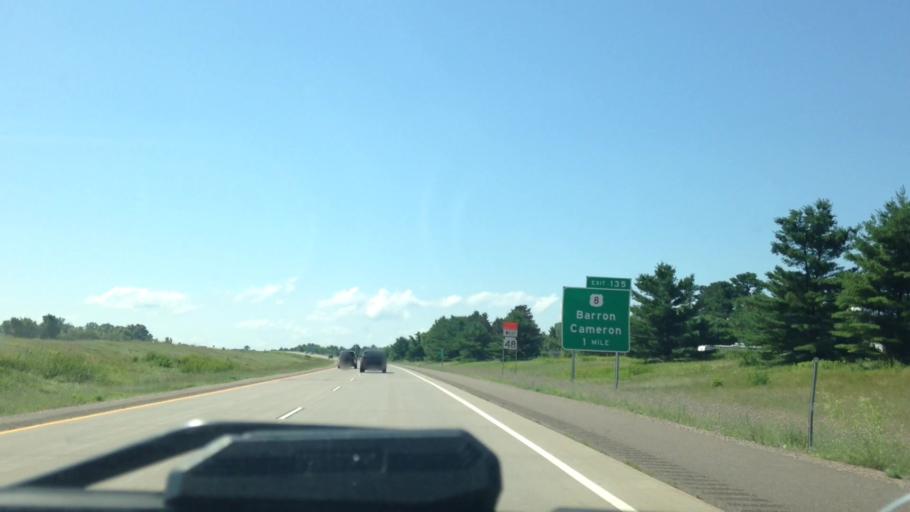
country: US
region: Wisconsin
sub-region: Barron County
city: Cameron
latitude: 45.4171
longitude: -91.7643
